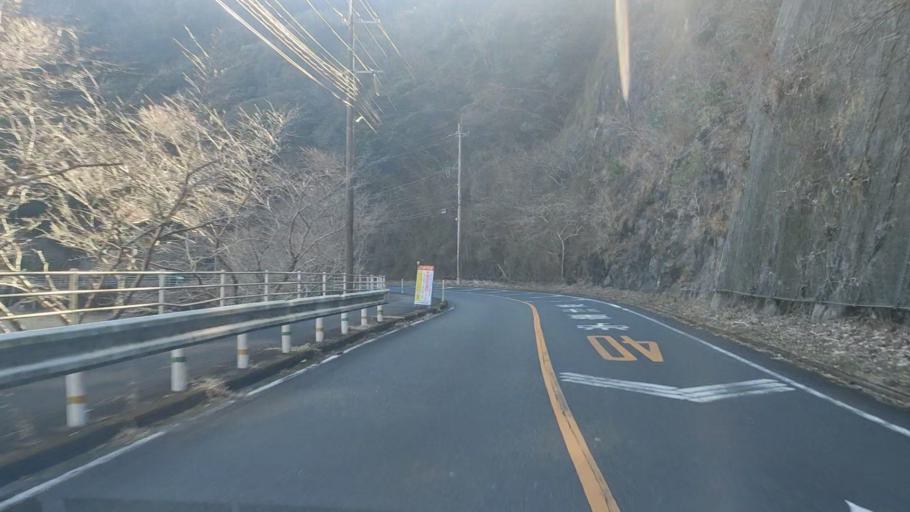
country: JP
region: Oita
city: Saiki
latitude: 32.7647
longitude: 131.7951
